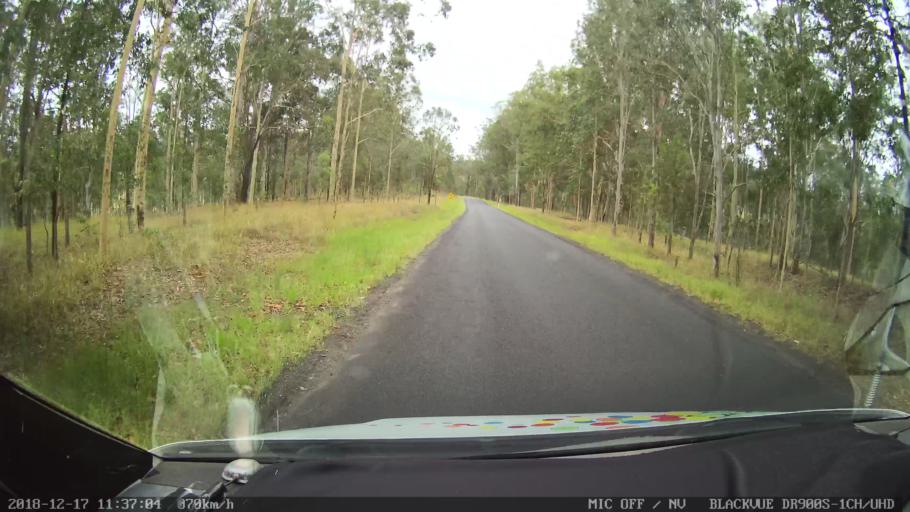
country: AU
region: New South Wales
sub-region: Kyogle
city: Kyogle
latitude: -28.7079
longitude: 152.6061
